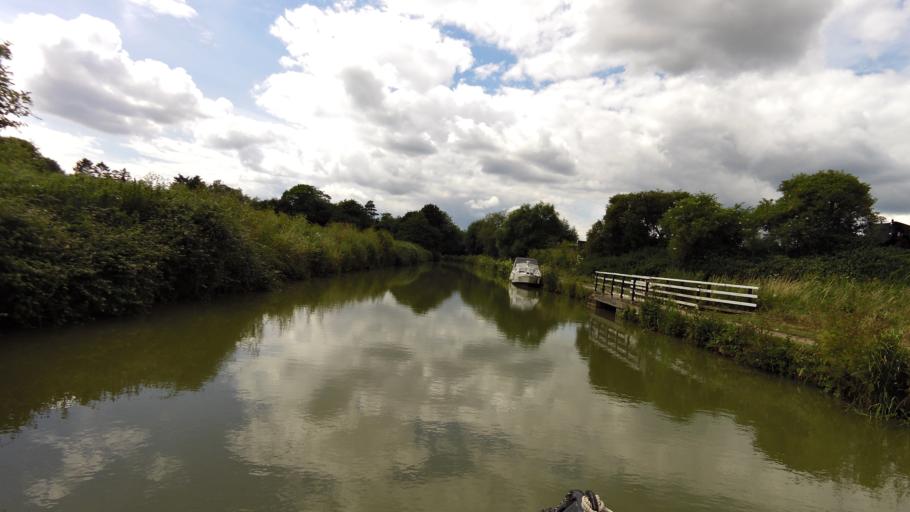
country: GB
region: England
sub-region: Wiltshire
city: Seend
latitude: 51.3559
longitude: -2.0617
